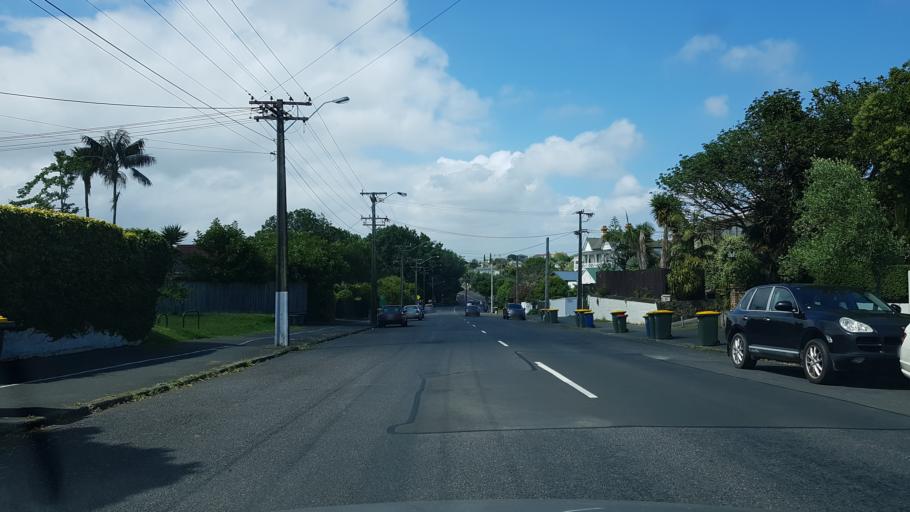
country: NZ
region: Auckland
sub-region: Auckland
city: Auckland
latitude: -36.8233
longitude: 174.8041
